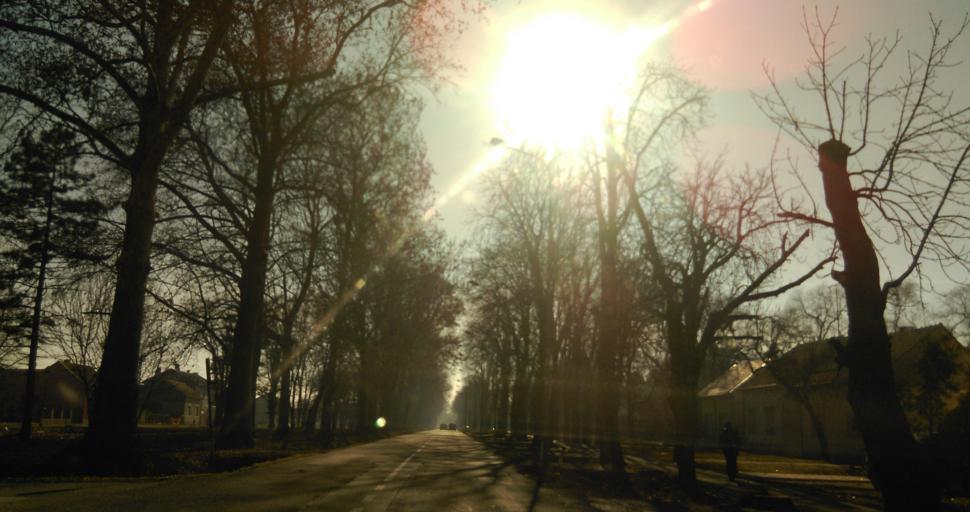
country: RS
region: Autonomna Pokrajina Vojvodina
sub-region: Sremski Okrug
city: Ruma
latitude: 45.0005
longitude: 19.8232
